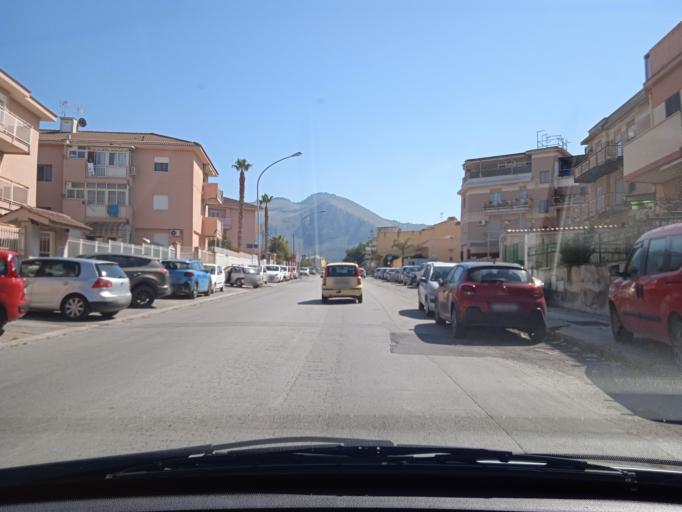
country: IT
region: Sicily
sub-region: Palermo
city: Villabate
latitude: 38.0894
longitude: 13.4326
